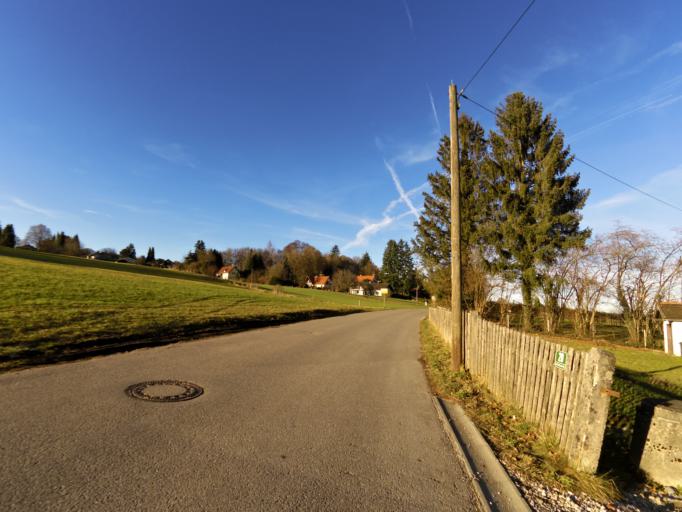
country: DE
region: Bavaria
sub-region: Upper Bavaria
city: Icking
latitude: 47.9600
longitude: 11.4382
